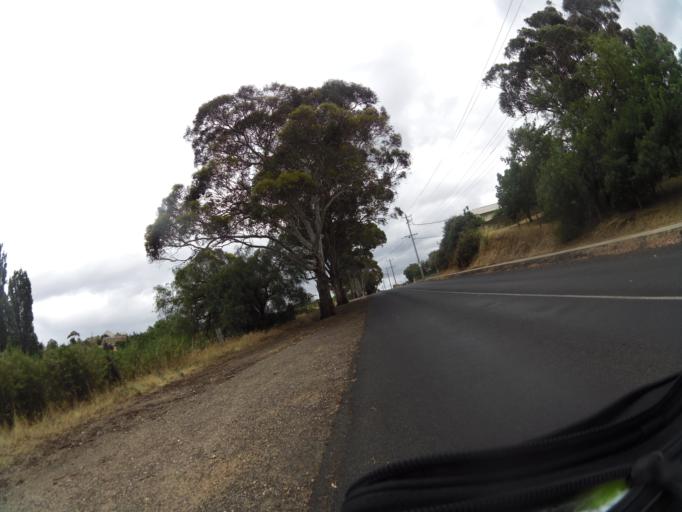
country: AU
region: Victoria
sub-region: Mount Alexander
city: Castlemaine
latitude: -37.0648
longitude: 144.2143
